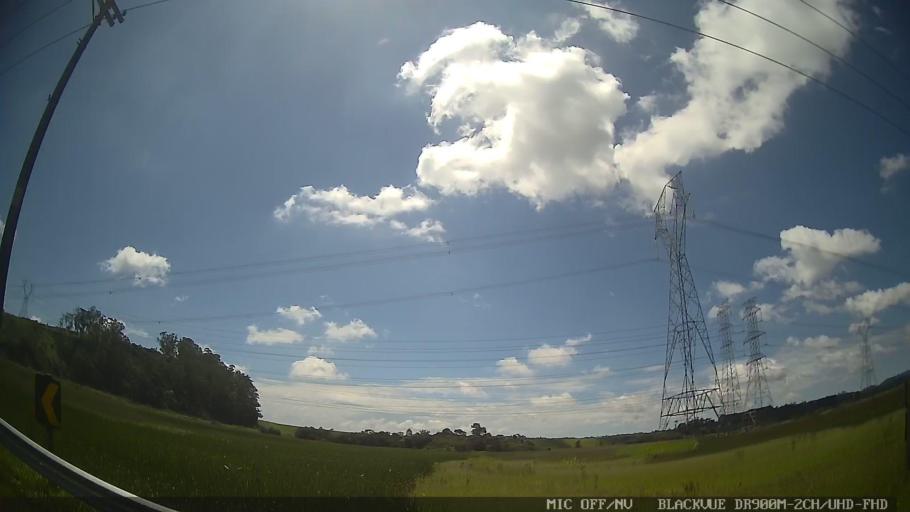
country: BR
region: Sao Paulo
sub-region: Mogi das Cruzes
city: Mogi das Cruzes
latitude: -23.6241
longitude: -46.2034
